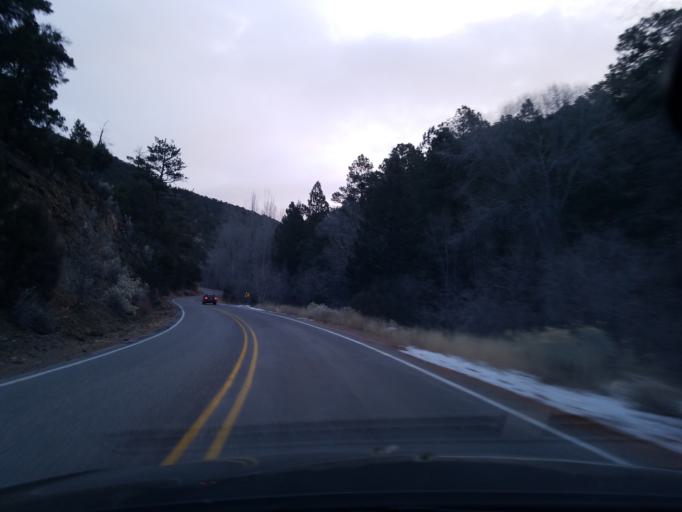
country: US
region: New Mexico
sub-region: Santa Fe County
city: Santa Fe
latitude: 35.7266
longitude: -105.8816
